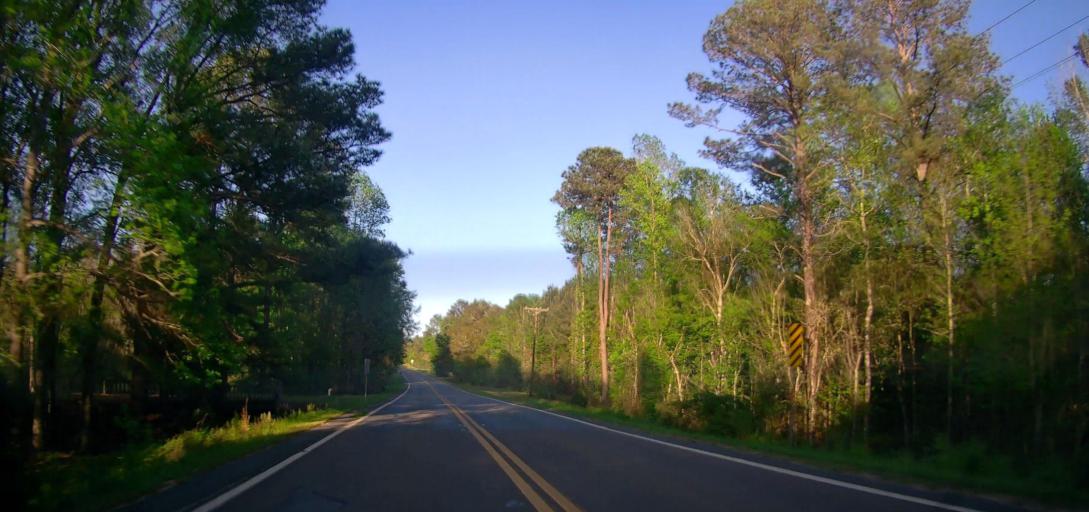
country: US
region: Georgia
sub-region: Schley County
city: Ellaville
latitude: 32.3167
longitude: -84.2532
